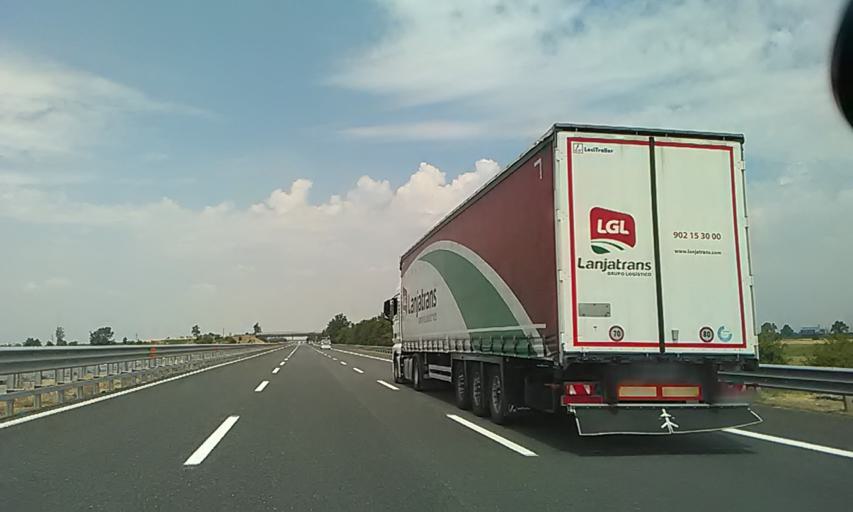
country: IT
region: Piedmont
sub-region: Provincia di Alessandria
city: Predosa
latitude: 44.7770
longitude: 8.6253
